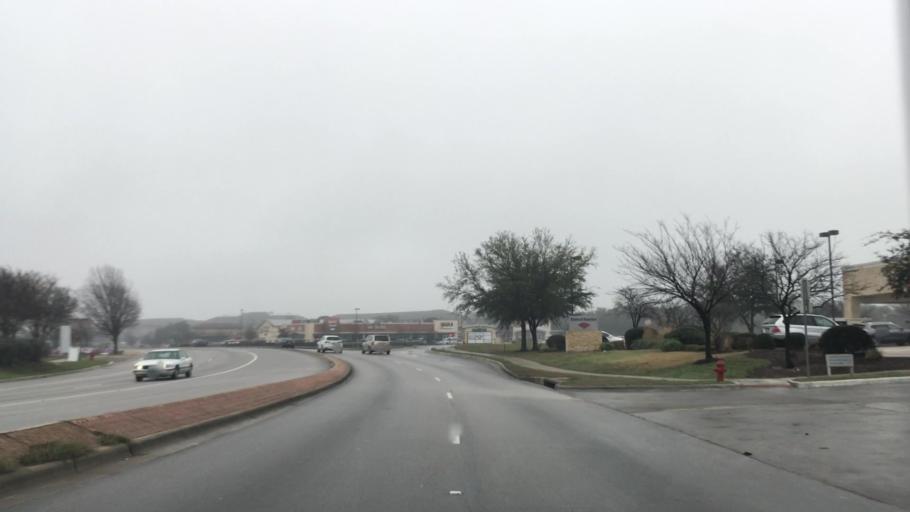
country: US
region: Texas
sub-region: Williamson County
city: Cedar Park
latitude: 30.4812
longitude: -97.8319
